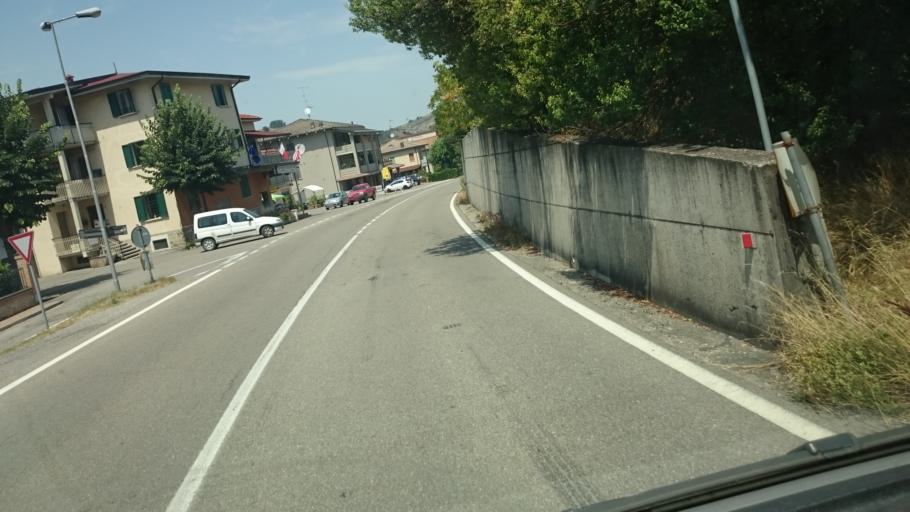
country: IT
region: Emilia-Romagna
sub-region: Provincia di Reggio Emilia
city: Vezzano sul Crostolo
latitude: 44.5603
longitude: 10.5288
